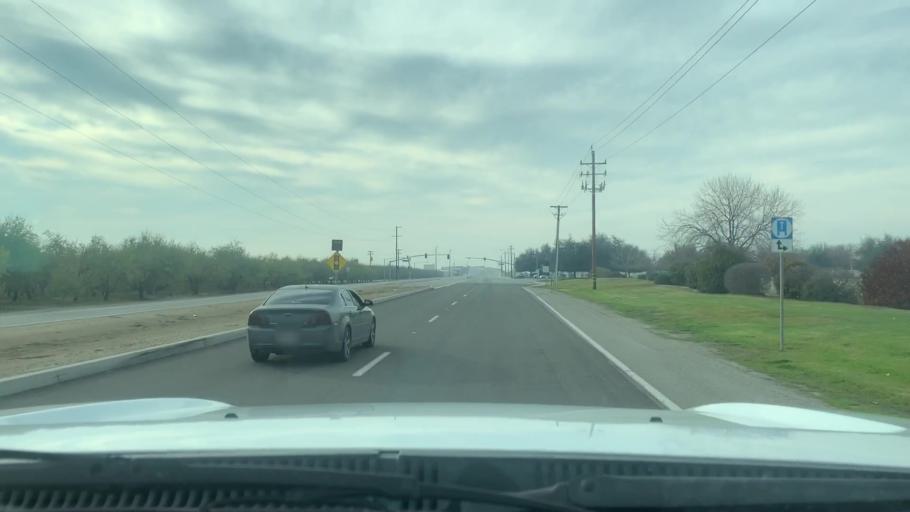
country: US
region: California
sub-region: Kern County
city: Rosedale
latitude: 35.4418
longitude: -119.1871
